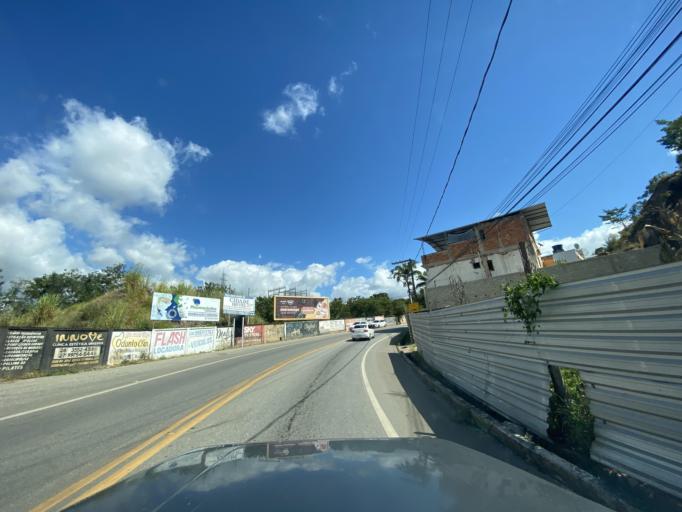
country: BR
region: Espirito Santo
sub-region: Alegre
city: Alegre
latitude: -20.7622
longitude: -41.5239
